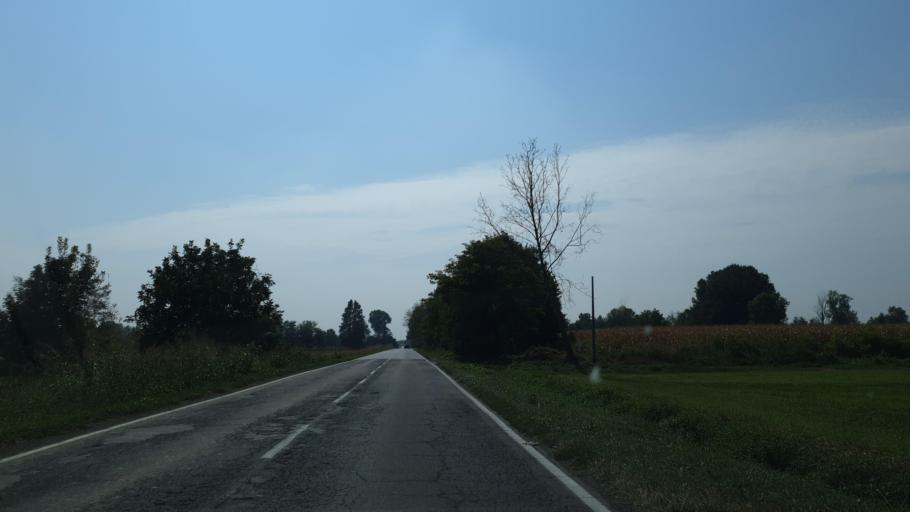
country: IT
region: Lombardy
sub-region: Provincia di Brescia
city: Milzano
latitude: 45.2659
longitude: 10.1919
